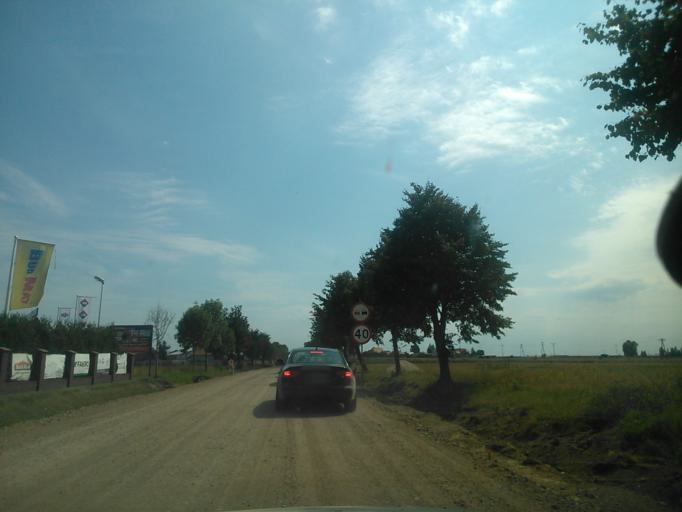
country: PL
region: Warmian-Masurian Voivodeship
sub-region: Powiat dzialdowski
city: Dzialdowo
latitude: 53.2229
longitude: 20.2050
